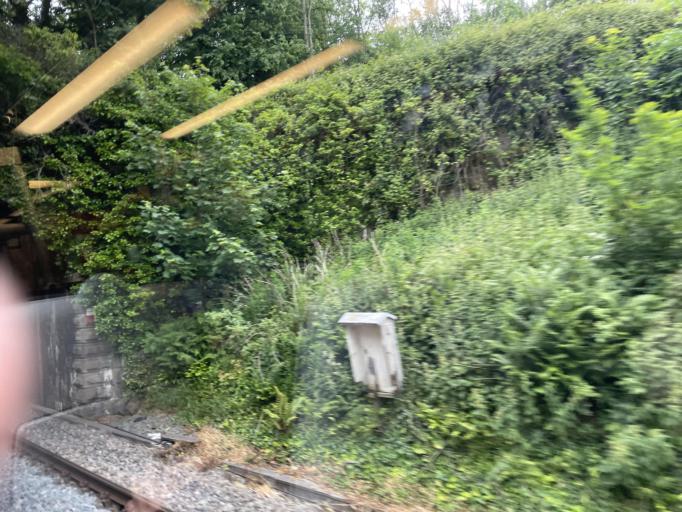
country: GB
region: Wales
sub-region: Anglesey
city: Beaumaris
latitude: 53.2178
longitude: -4.0867
